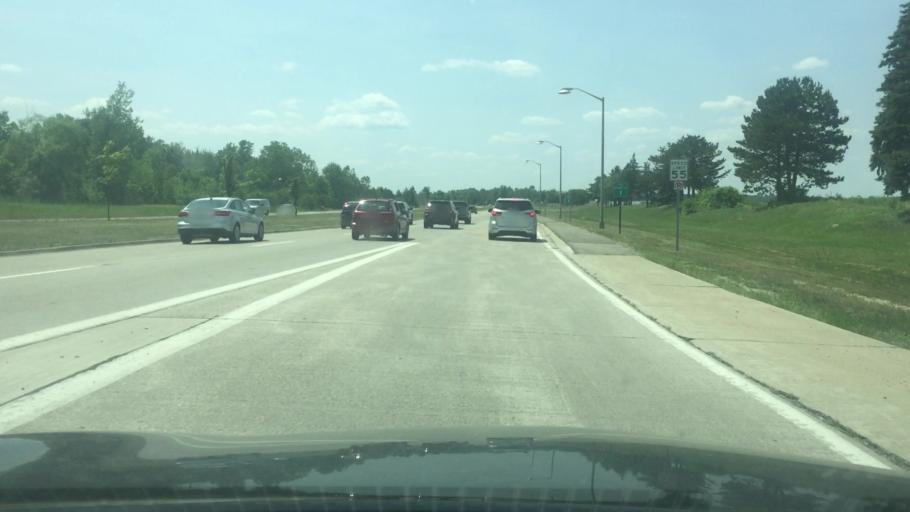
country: US
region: Michigan
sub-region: Wayne County
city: Romulus
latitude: 42.1934
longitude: -83.3684
